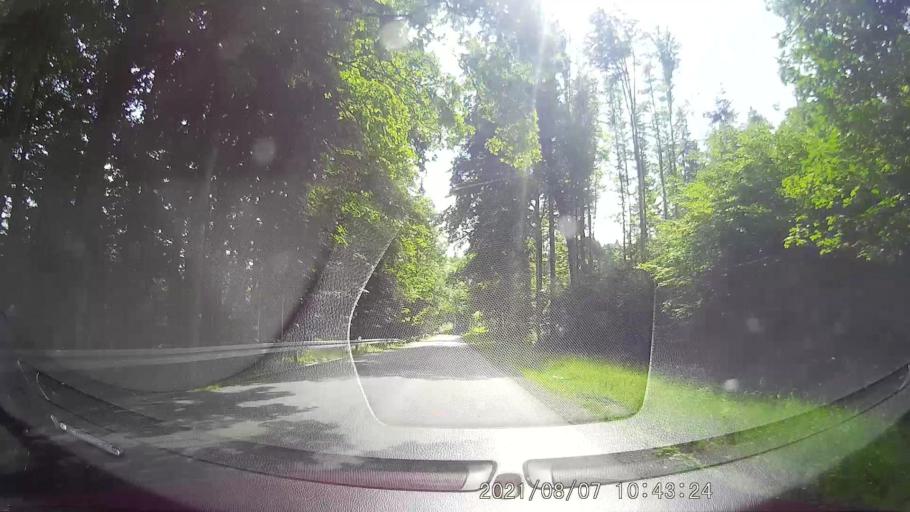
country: PL
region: Lower Silesian Voivodeship
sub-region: Powiat klodzki
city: Duszniki-Zdroj
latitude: 50.3279
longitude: 16.3961
